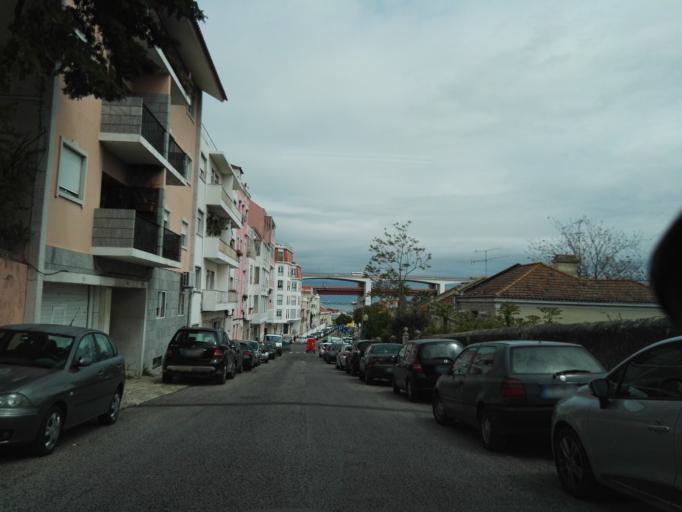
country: PT
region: Setubal
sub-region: Almada
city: Pragal
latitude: 38.7029
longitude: -9.1854
